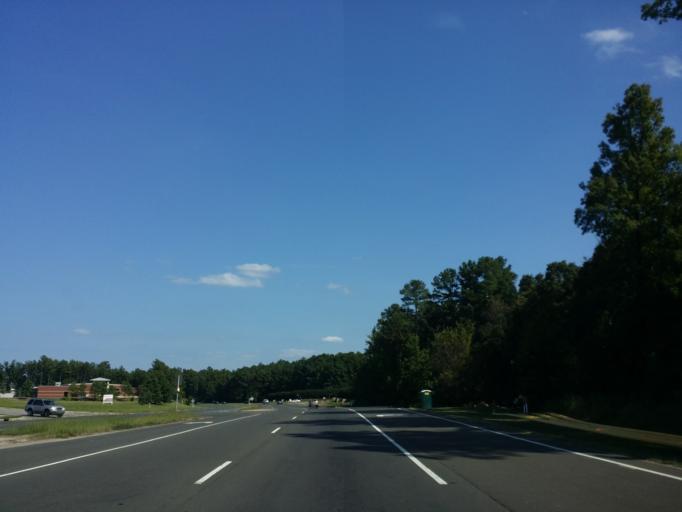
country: US
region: North Carolina
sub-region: Durham County
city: Durham
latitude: 35.9233
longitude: -78.8448
